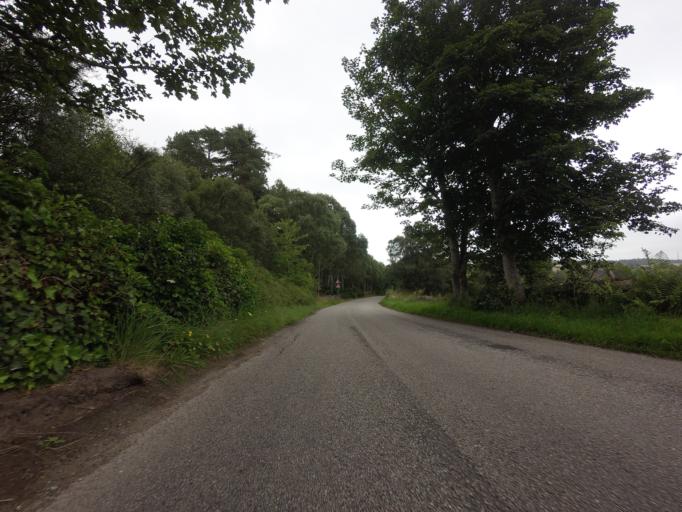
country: GB
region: Scotland
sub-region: Highland
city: Evanton
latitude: 57.8872
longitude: -4.3887
